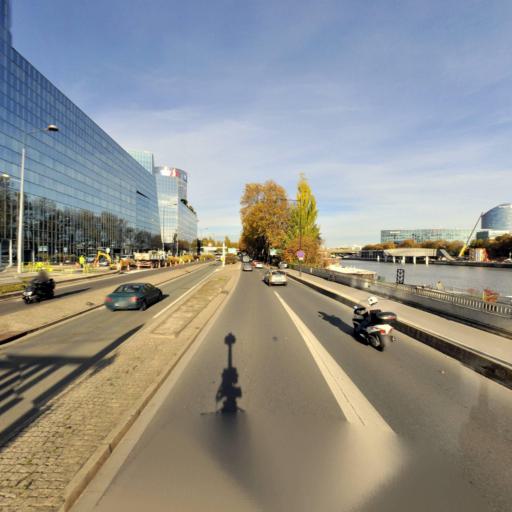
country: FR
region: Ile-de-France
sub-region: Departement des Hauts-de-Seine
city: Boulogne-Billancourt
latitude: 48.8323
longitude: 2.2599
